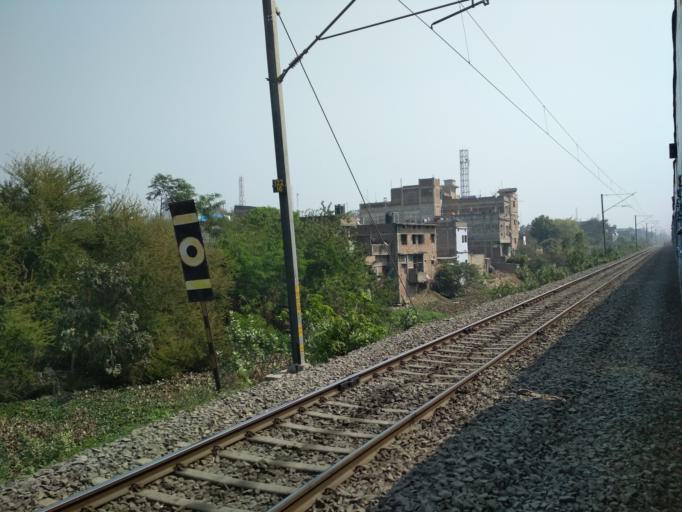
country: IN
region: Bihar
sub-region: Khagaria
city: Khagaria
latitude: 25.5068
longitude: 86.4798
